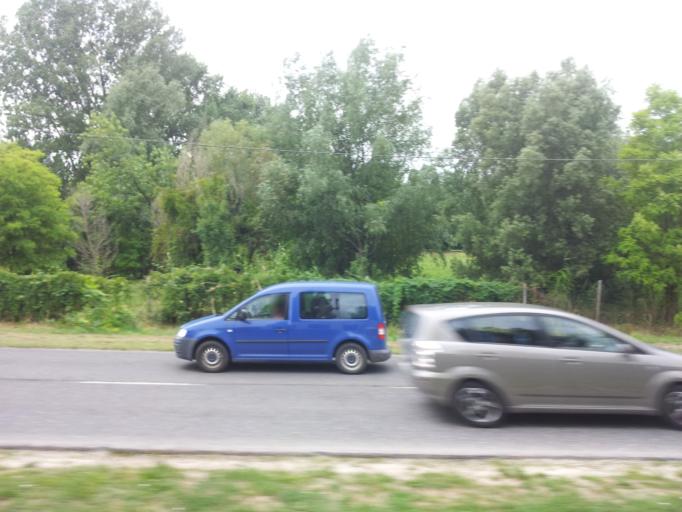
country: HU
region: Veszprem
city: Balatonalmadi
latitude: 47.0186
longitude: 18.0077
